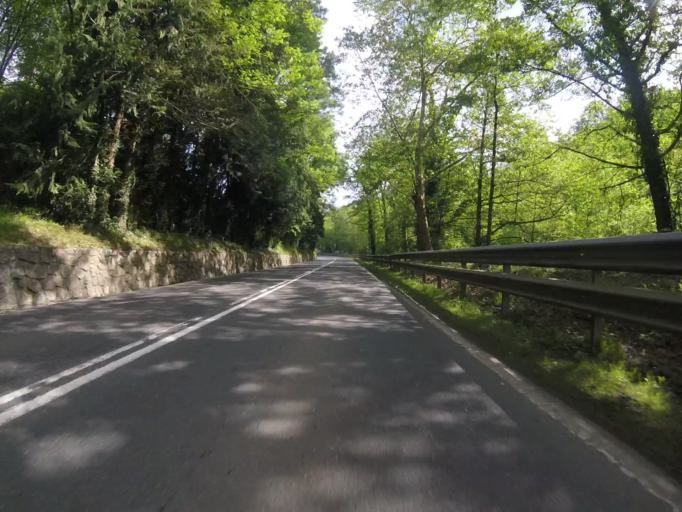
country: ES
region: Basque Country
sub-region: Provincia de Guipuzcoa
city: Azkoitia
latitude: 43.1621
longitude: -2.3317
